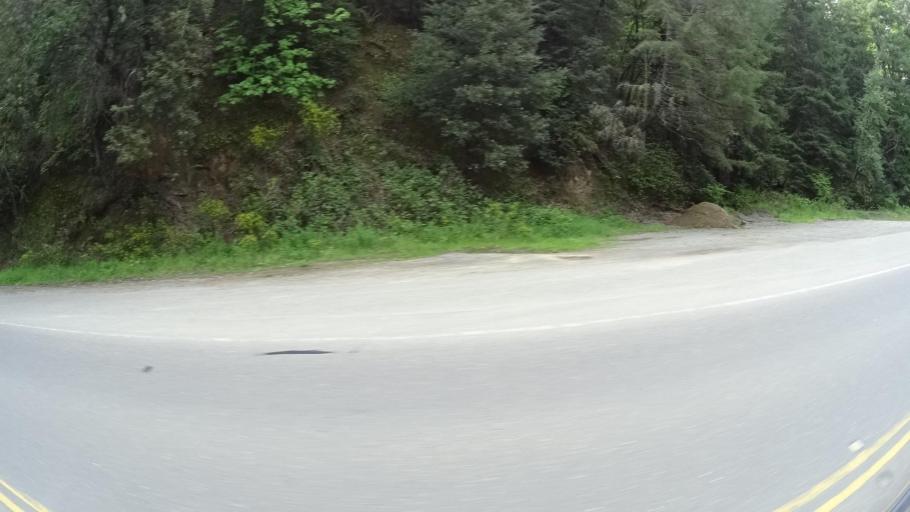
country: US
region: California
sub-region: Humboldt County
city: Redway
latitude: 40.1262
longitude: -123.8220
